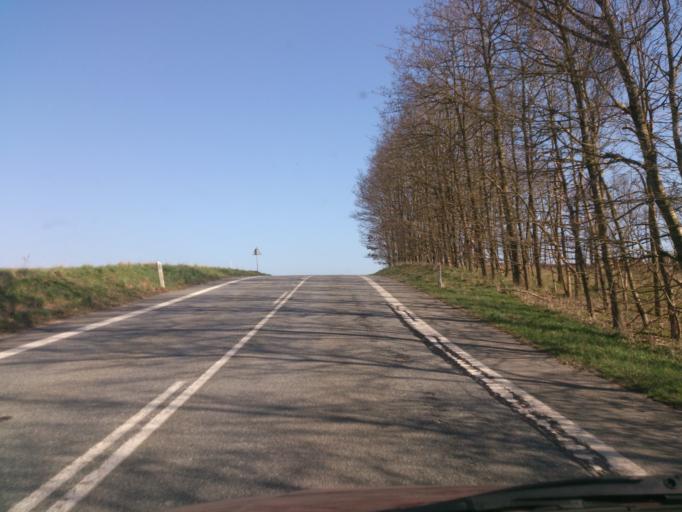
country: DK
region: Central Jutland
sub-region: Favrskov Kommune
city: Ulstrup
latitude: 56.4501
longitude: 9.7266
